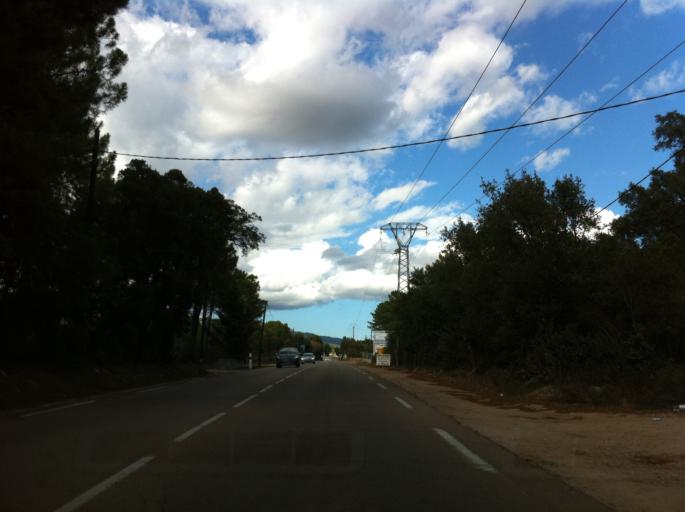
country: FR
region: Corsica
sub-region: Departement de la Corse-du-Sud
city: Porto-Vecchio
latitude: 41.6276
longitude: 9.2914
